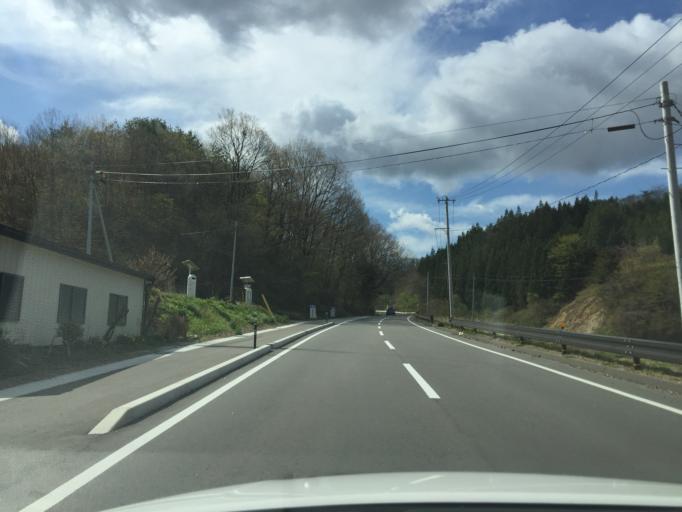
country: JP
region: Fukushima
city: Funehikimachi-funehiki
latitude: 37.6223
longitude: 140.6455
